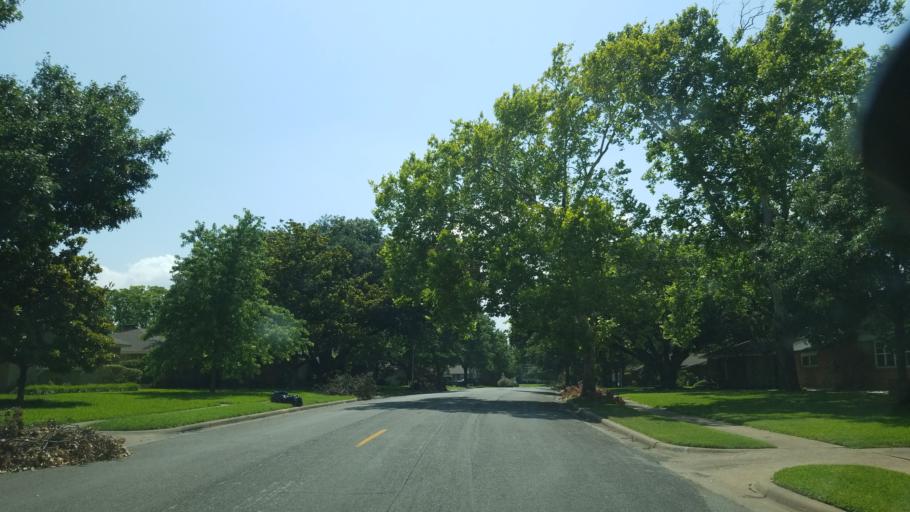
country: US
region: Texas
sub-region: Dallas County
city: Farmers Branch
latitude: 32.8875
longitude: -96.8610
